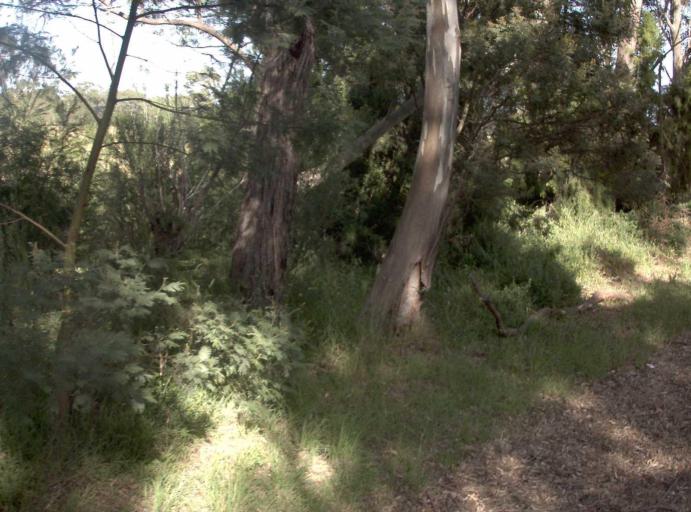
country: AU
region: Victoria
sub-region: East Gippsland
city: Lakes Entrance
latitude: -37.8076
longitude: 147.8421
